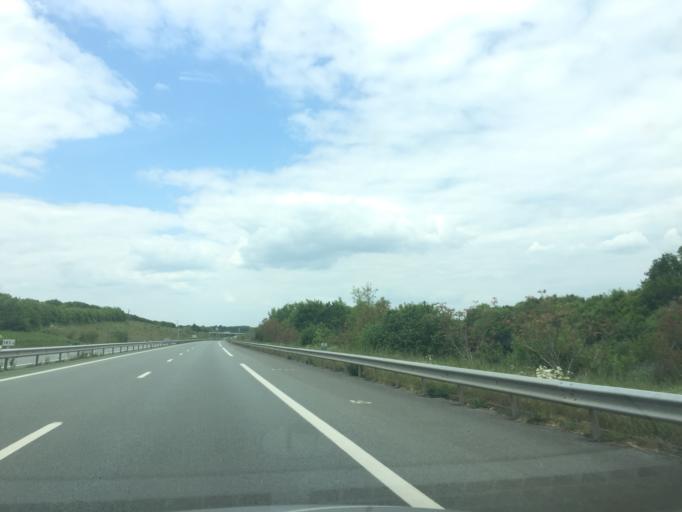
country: FR
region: Poitou-Charentes
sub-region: Departement des Deux-Sevres
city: Chauray
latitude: 46.3649
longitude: -0.3493
